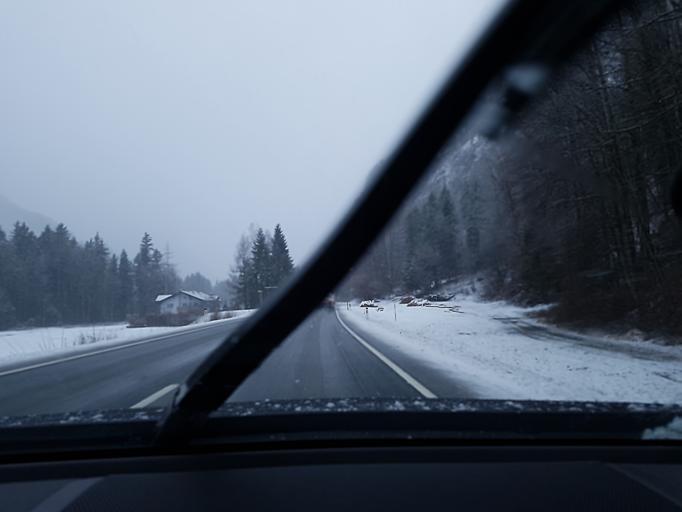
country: AT
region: Salzburg
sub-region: Politischer Bezirk Hallein
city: Scheffau am Tennengebirge
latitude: 47.5802
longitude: 13.2526
